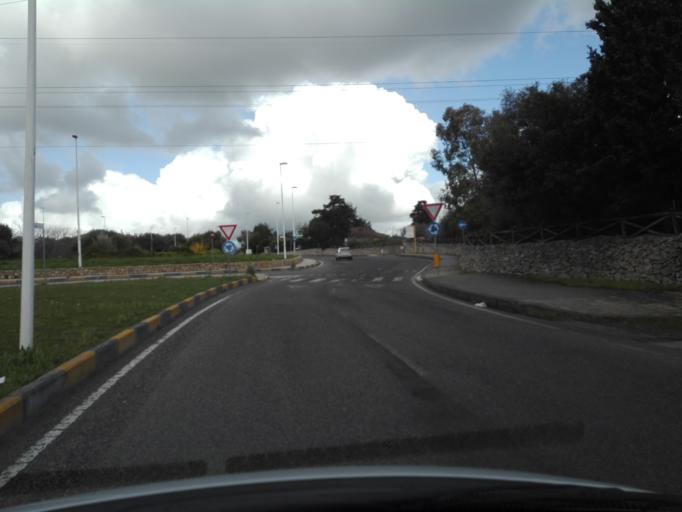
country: IT
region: Sardinia
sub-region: Provincia di Sassari
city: Sassari
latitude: 40.7113
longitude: 8.5823
